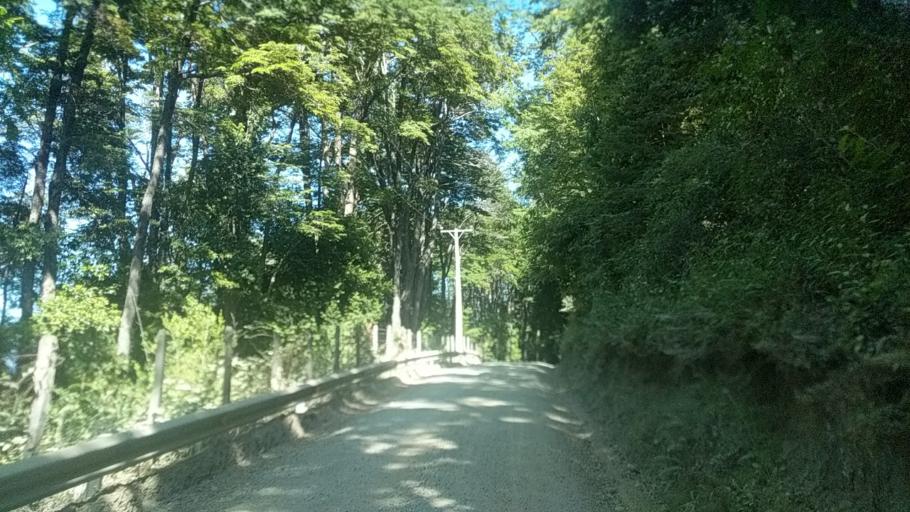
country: CL
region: Araucania
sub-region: Provincia de Cautin
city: Pucon
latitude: -39.0641
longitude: -71.7303
